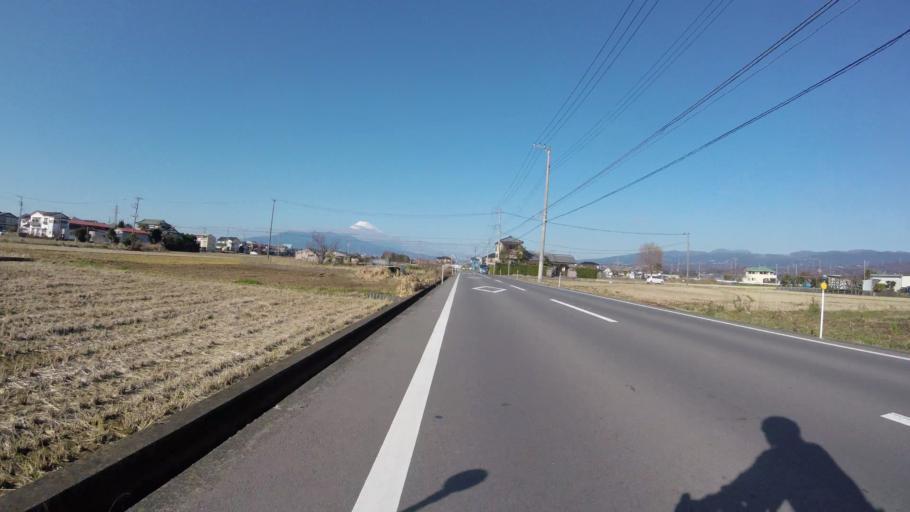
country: JP
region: Shizuoka
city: Mishima
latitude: 35.0642
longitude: 138.9513
